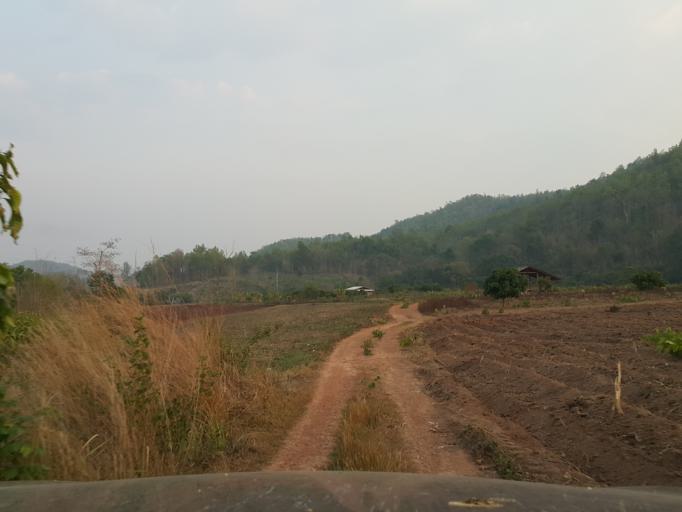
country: TH
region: Lamphun
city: Thung Hua Chang
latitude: 17.9127
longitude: 99.0743
